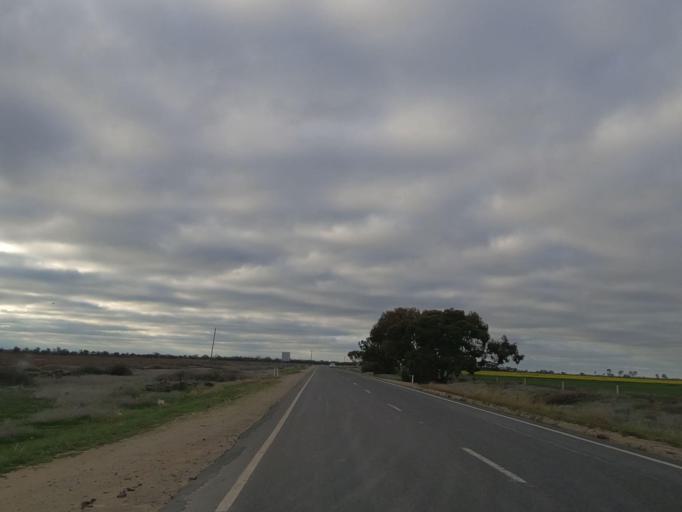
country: AU
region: Victoria
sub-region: Swan Hill
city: Swan Hill
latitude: -35.8310
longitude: 143.9442
